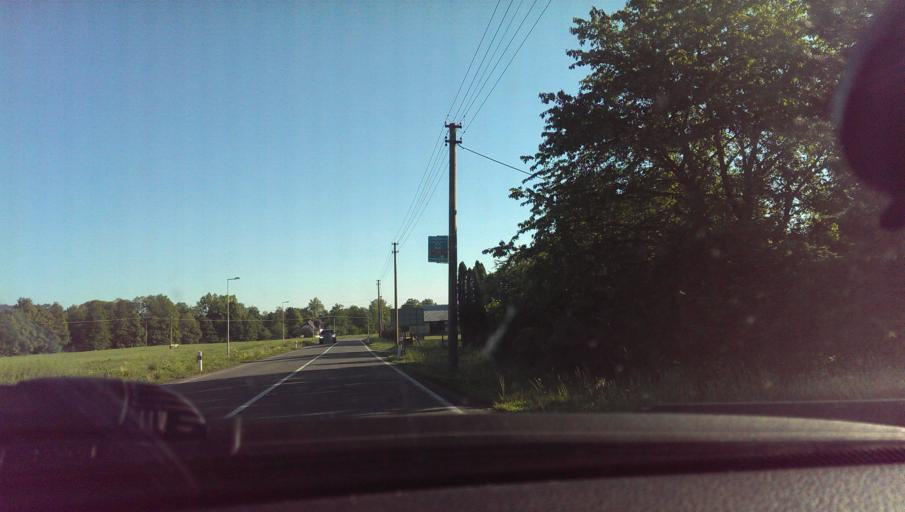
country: CZ
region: Moravskoslezsky
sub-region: Okres Frydek-Mistek
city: Celadna
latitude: 49.5539
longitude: 18.3432
